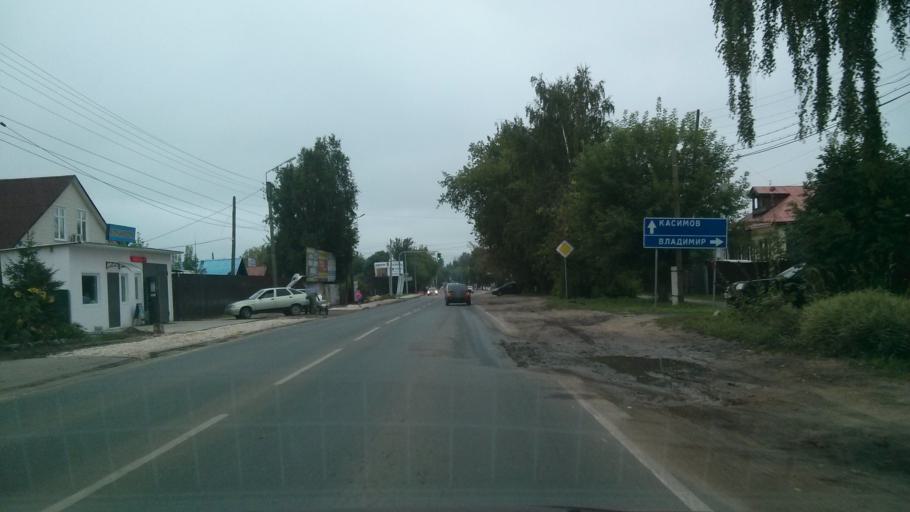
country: RU
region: Vladimir
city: Murom
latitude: 55.5888
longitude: 42.0356
